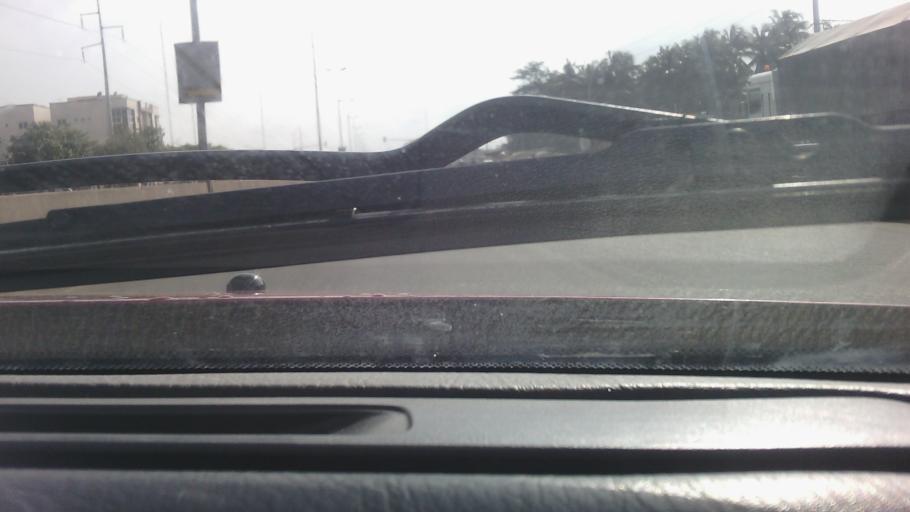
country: BJ
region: Littoral
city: Cotonou
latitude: 6.3693
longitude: 2.4889
